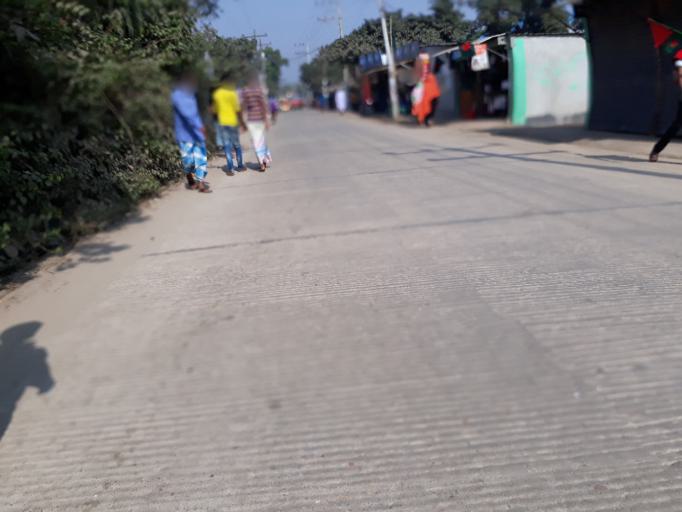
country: BD
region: Dhaka
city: Tungi
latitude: 23.8819
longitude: 90.3099
